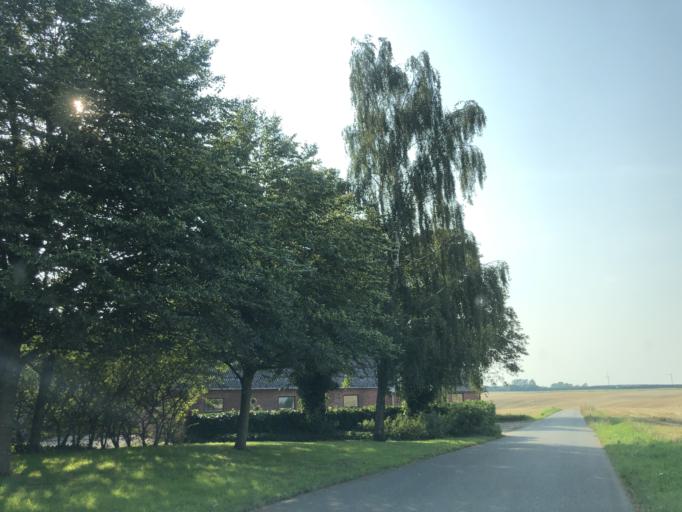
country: DK
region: Central Jutland
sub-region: Favrskov Kommune
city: Hammel
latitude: 56.2445
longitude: 9.7754
